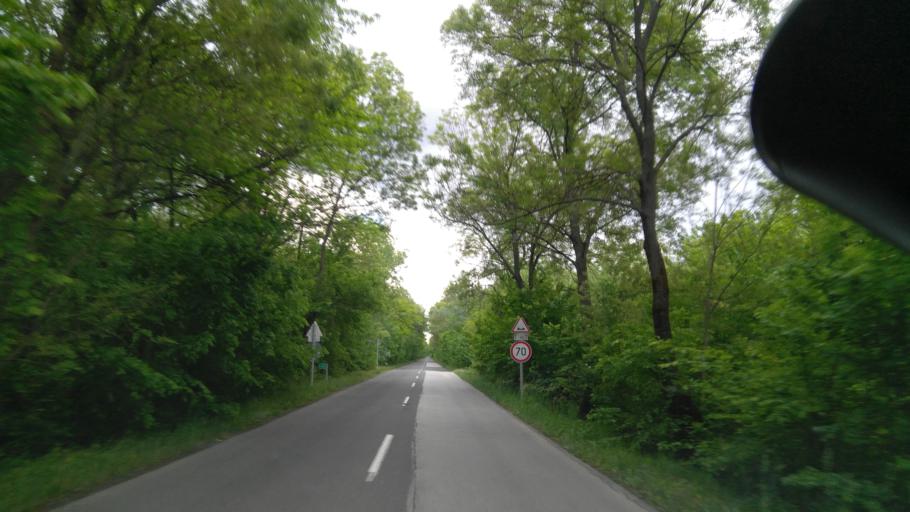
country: HU
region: Bekes
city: Bucsa
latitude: 47.1772
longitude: 21.0577
